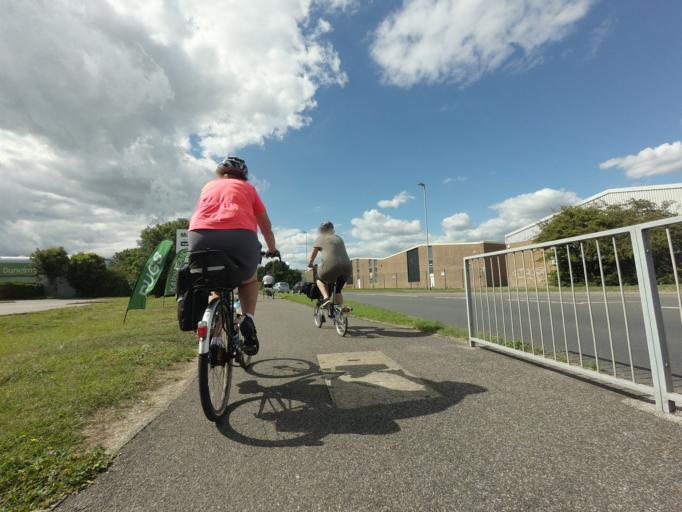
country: GB
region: England
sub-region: East Sussex
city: Eastbourne
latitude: 50.7946
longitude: 0.2876
